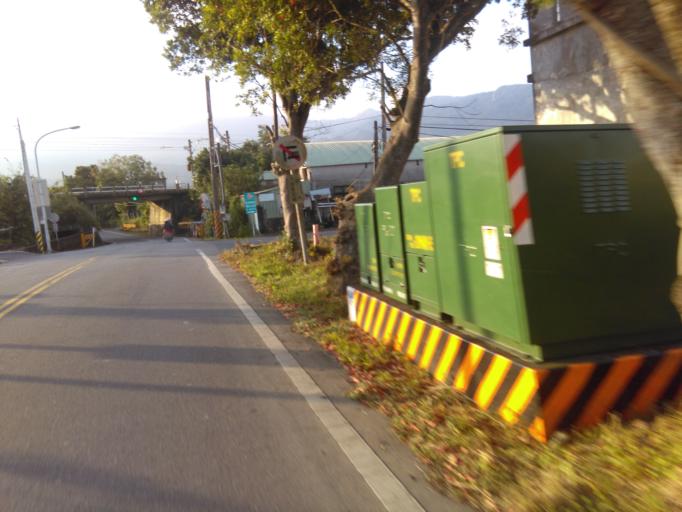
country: TW
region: Taiwan
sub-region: Yilan
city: Yilan
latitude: 24.8084
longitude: 121.7690
